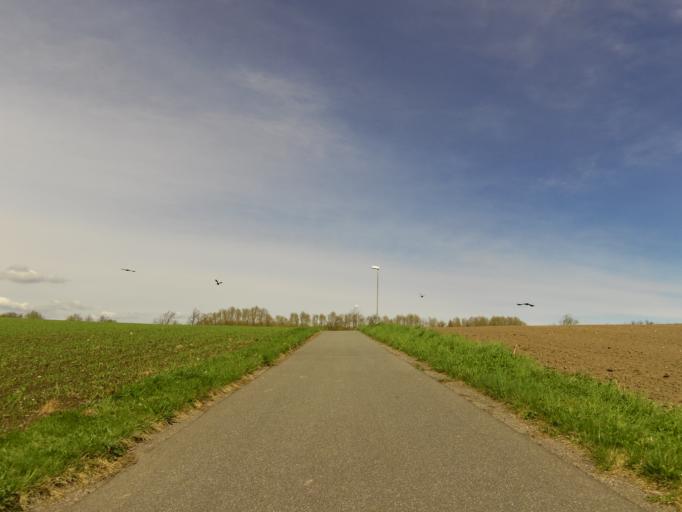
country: DK
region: Central Jutland
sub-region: Skive Kommune
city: Skive
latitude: 56.5857
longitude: 9.0195
